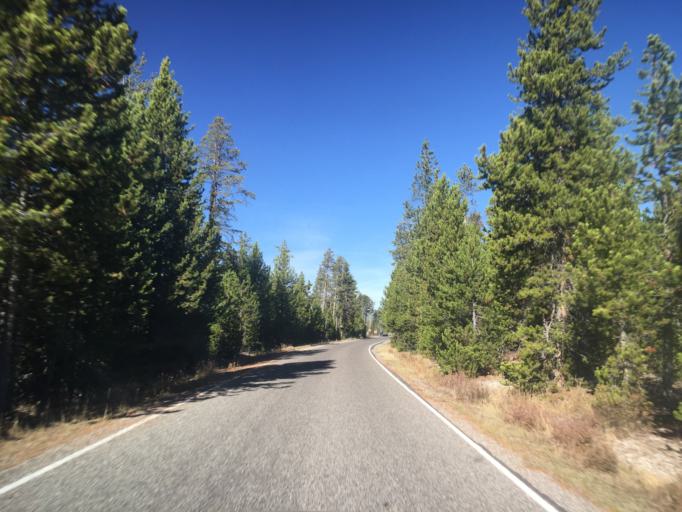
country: US
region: Montana
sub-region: Gallatin County
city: West Yellowstone
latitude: 44.5476
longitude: -110.8046
